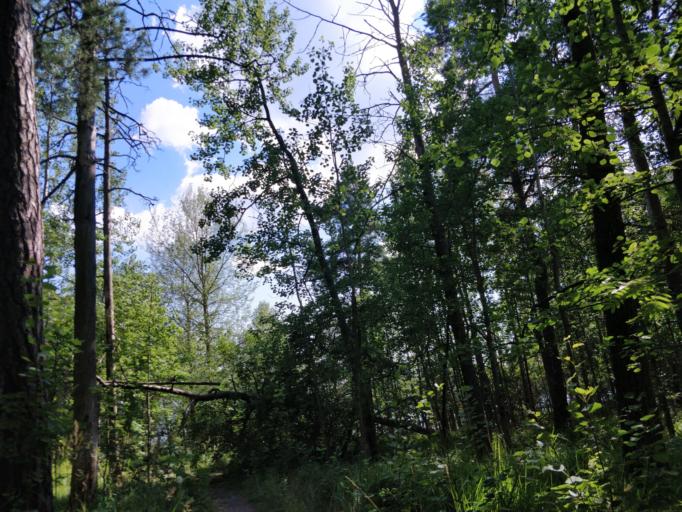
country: FI
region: Uusimaa
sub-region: Helsinki
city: Helsinki
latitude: 60.1798
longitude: 24.9933
